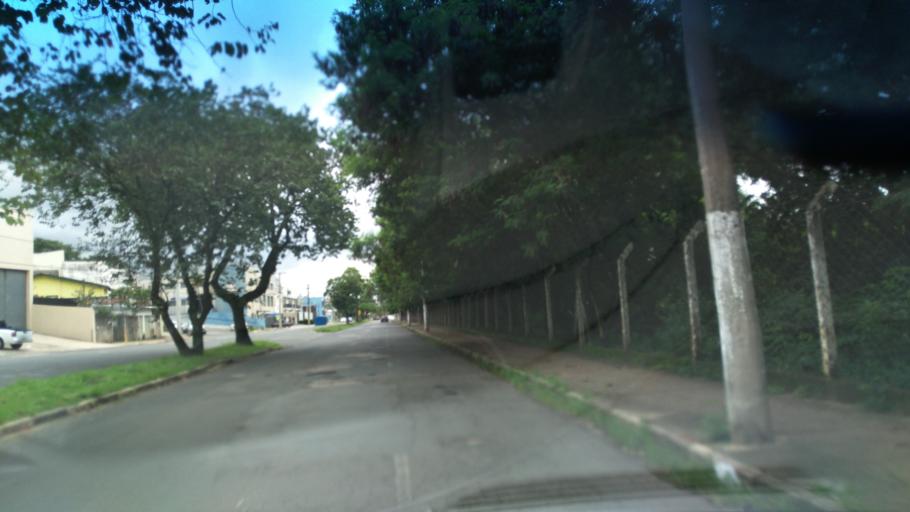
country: BR
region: Sao Paulo
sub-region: Valinhos
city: Valinhos
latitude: -22.9599
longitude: -46.9791
